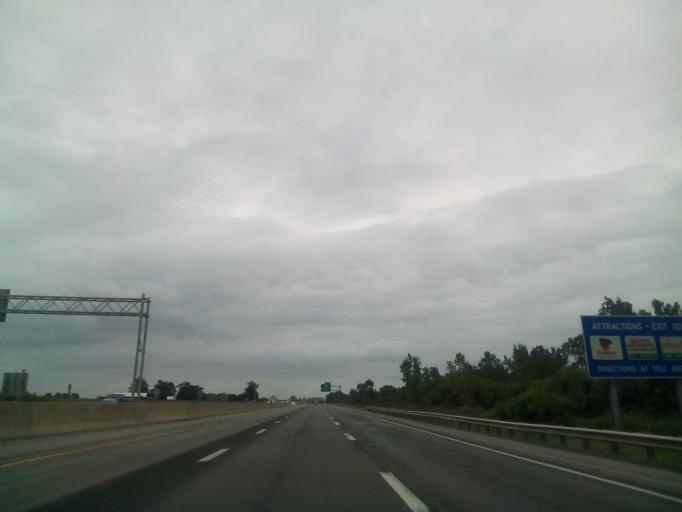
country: US
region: Ohio
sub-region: Huron County
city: Bellevue
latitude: 41.3431
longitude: -82.7784
